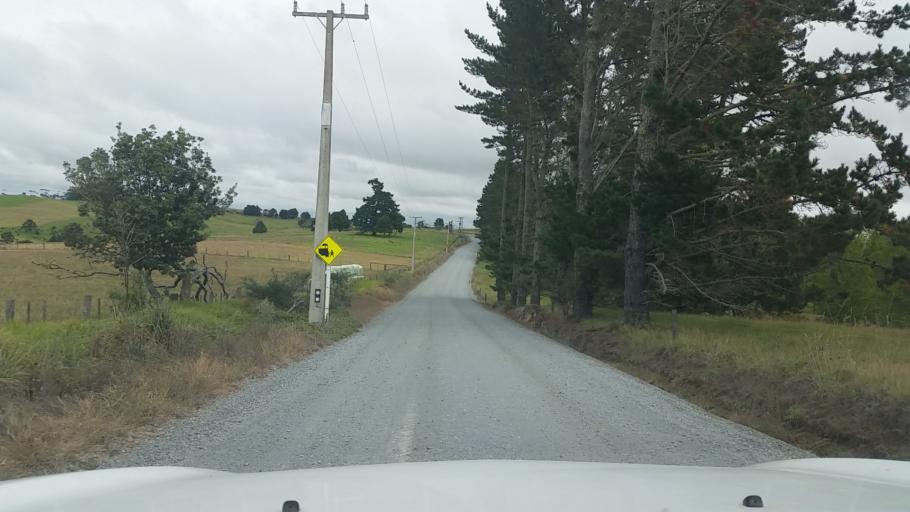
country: NZ
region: Northland
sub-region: Whangarei
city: Maungatapere
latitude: -35.6637
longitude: 174.1831
